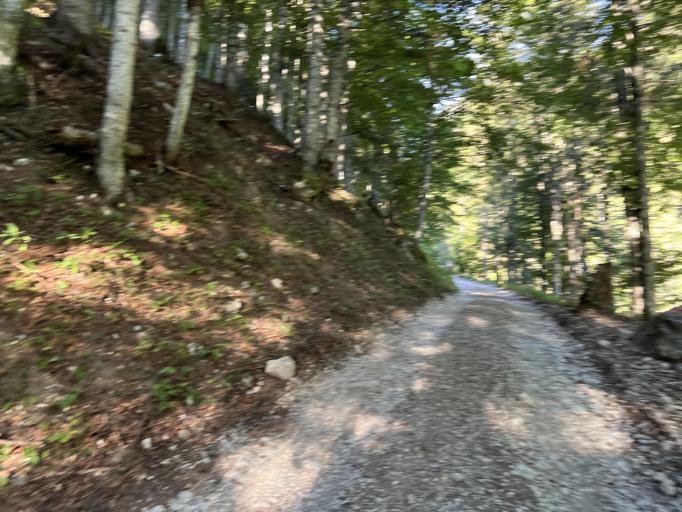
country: IT
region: Friuli Venezia Giulia
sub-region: Provincia di Udine
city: Forni Avoltri
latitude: 46.6104
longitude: 12.7923
